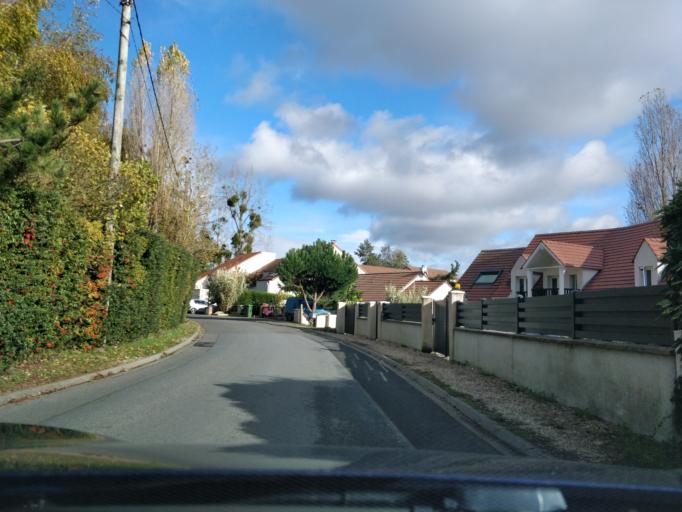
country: FR
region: Ile-de-France
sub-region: Departement de l'Essonne
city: Fontenay-les-Briis
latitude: 48.6217
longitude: 2.1587
